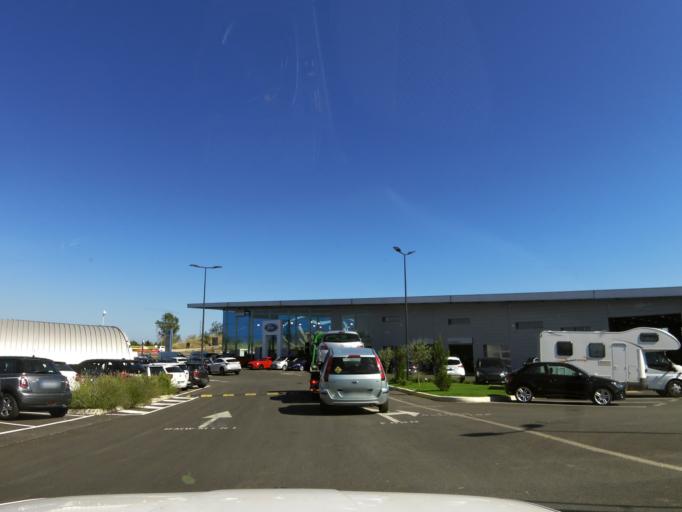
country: FR
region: Languedoc-Roussillon
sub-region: Departement de l'Herault
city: Lattes
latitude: 43.5744
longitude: 3.8727
